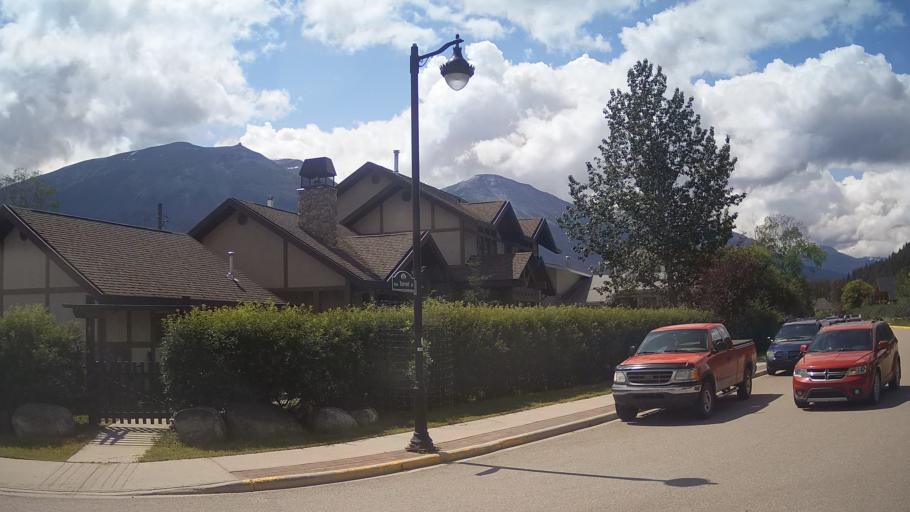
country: CA
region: Alberta
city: Jasper Park Lodge
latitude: 52.8741
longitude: -118.0864
